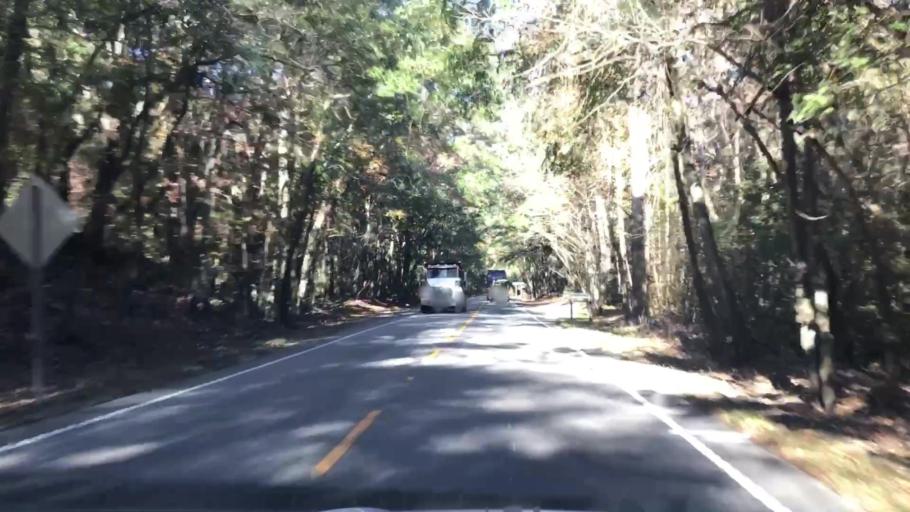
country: US
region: South Carolina
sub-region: Charleston County
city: Shell Point
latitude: 32.8628
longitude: -80.0808
